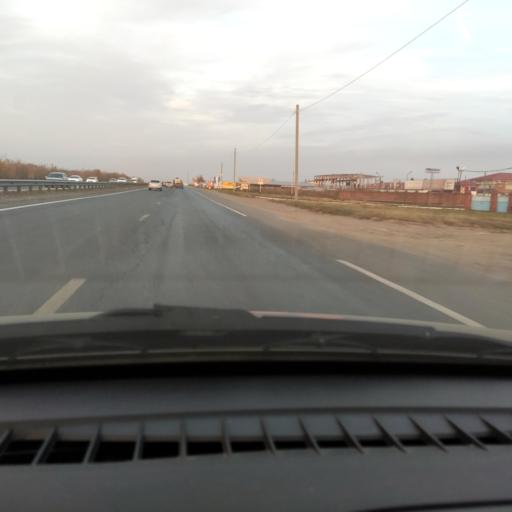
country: RU
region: Samara
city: Tol'yatti
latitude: 53.5635
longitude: 49.3661
